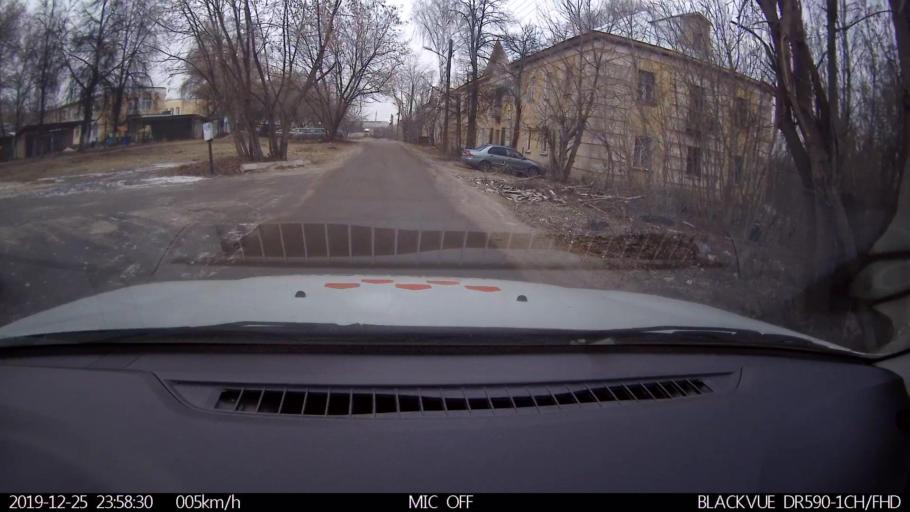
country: RU
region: Nizjnij Novgorod
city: Gorbatovka
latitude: 56.3418
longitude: 43.8283
